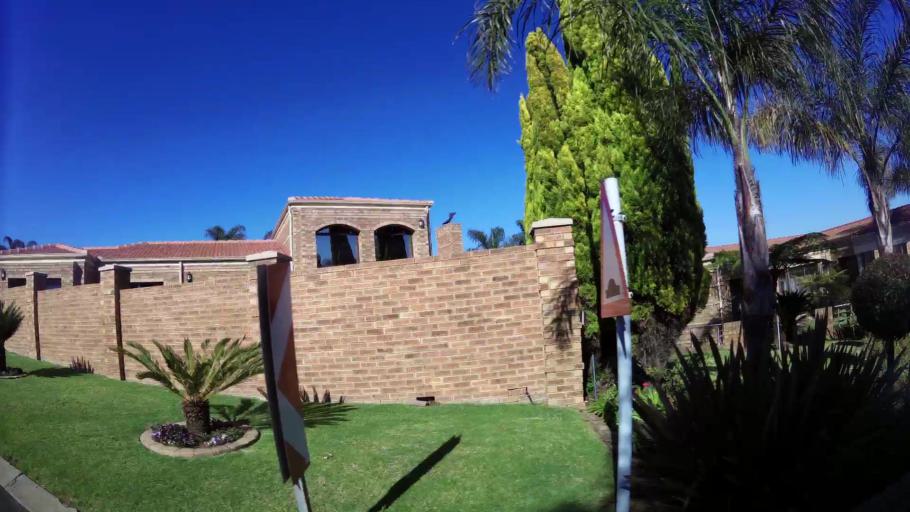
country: ZA
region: Mpumalanga
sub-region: Nkangala District Municipality
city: Witbank
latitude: -25.8907
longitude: 29.2497
